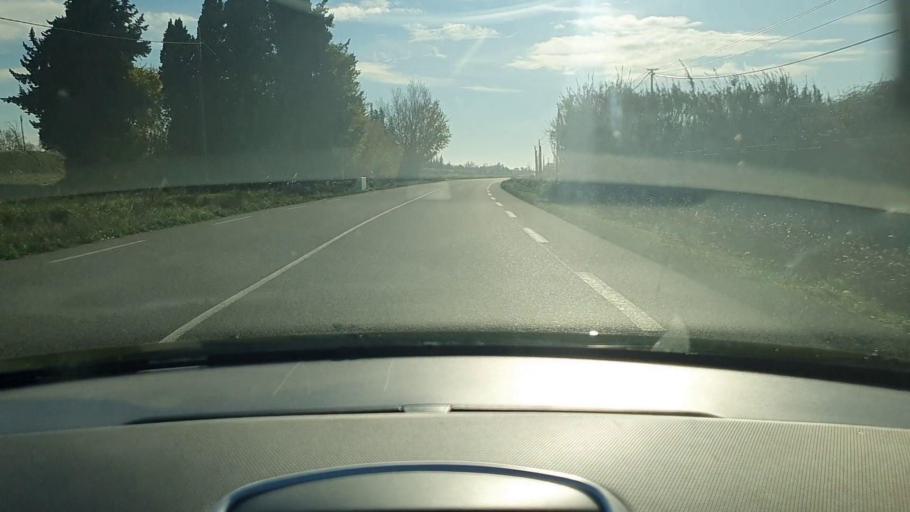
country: FR
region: Languedoc-Roussillon
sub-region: Departement du Gard
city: Fourques
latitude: 43.7369
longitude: 4.6114
